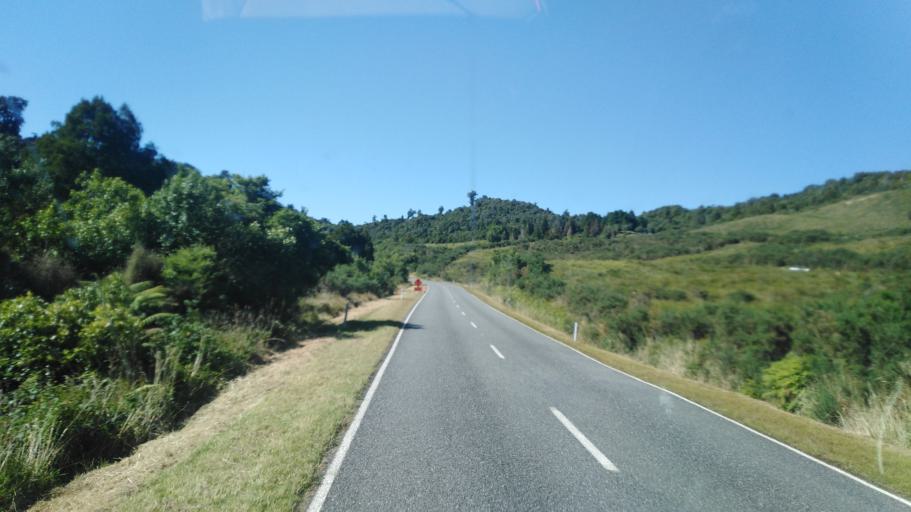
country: NZ
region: West Coast
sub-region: Buller District
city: Westport
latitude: -41.5318
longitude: 171.9903
